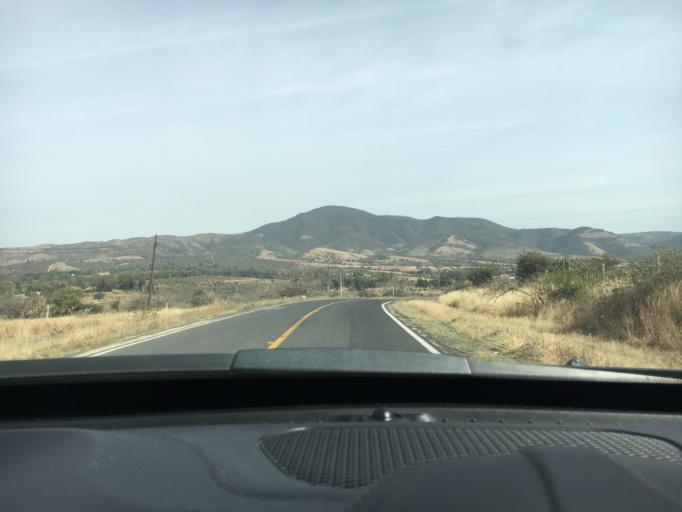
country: MX
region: Guanajuato
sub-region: Silao de la Victoria
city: San Francisco (Banos de Agua Caliente)
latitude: 21.0729
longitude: -101.4915
